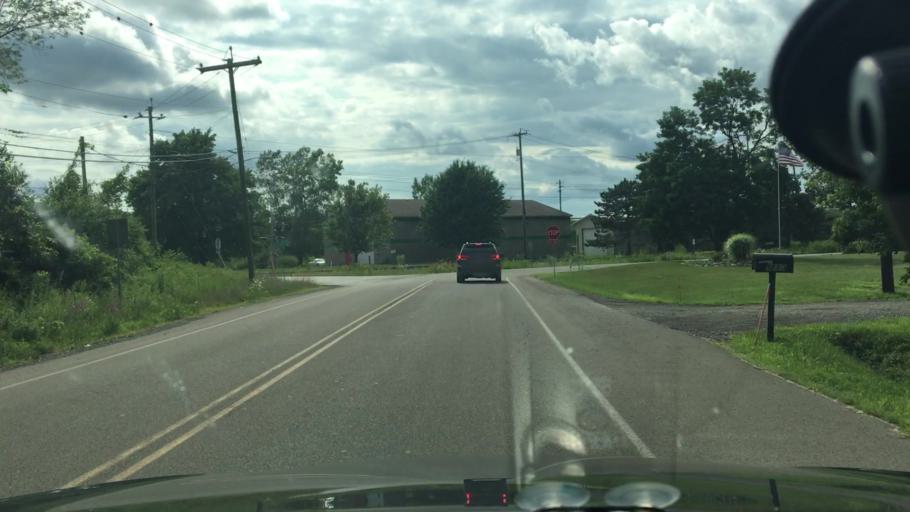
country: US
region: New York
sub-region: Erie County
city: Orchard Park
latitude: 42.7708
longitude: -78.7646
